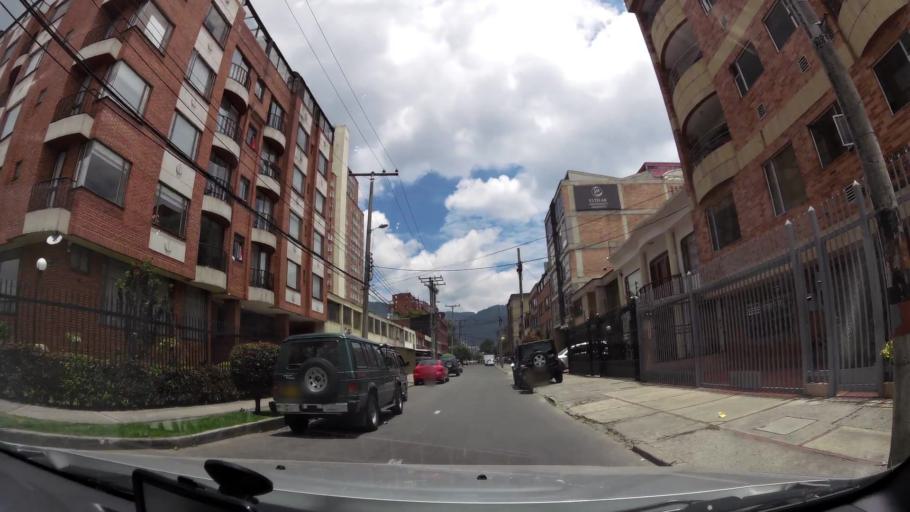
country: CO
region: Bogota D.C.
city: Bogota
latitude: 4.6339
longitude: -74.0906
